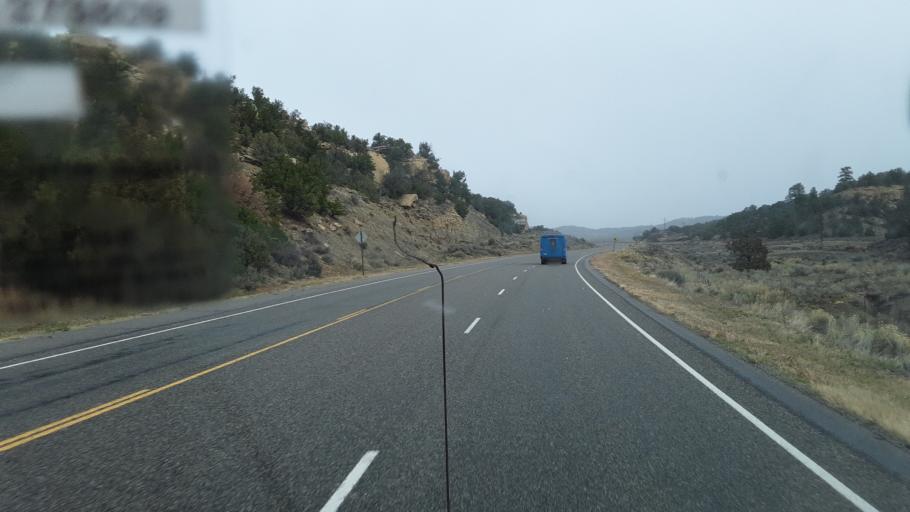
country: US
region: New Mexico
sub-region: Rio Arriba County
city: Tierra Amarilla
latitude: 36.4315
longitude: -106.4775
